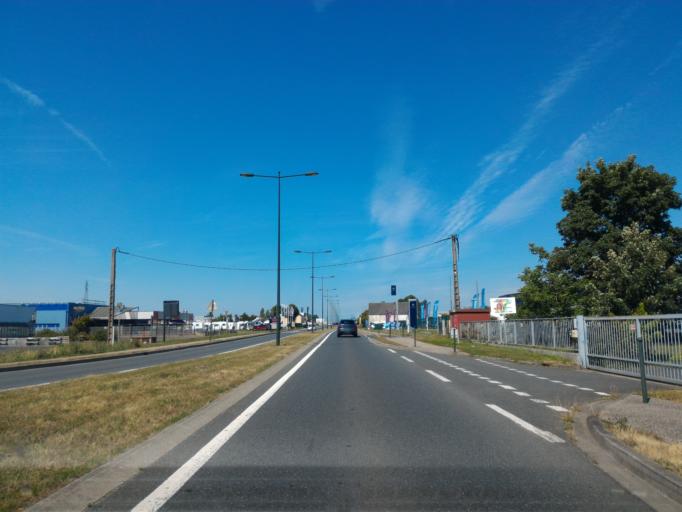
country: FR
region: Centre
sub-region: Departement de l'Indre
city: Saint-Maur
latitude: 46.7825
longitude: 1.6547
